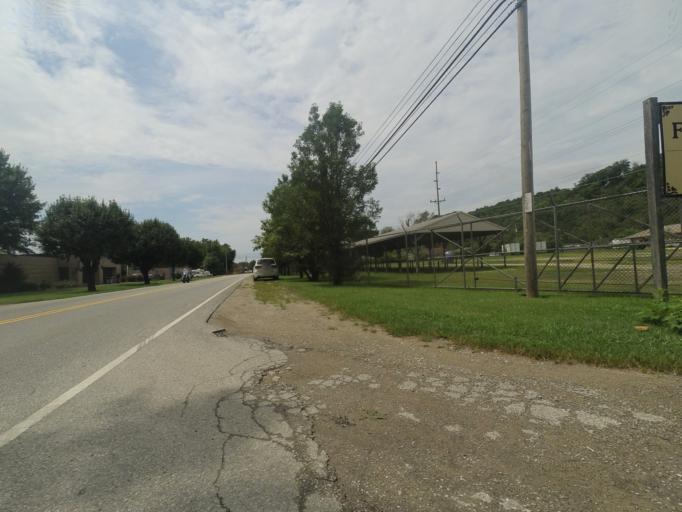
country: US
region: West Virginia
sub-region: Cabell County
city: Huntington
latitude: 38.4246
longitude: -82.4723
